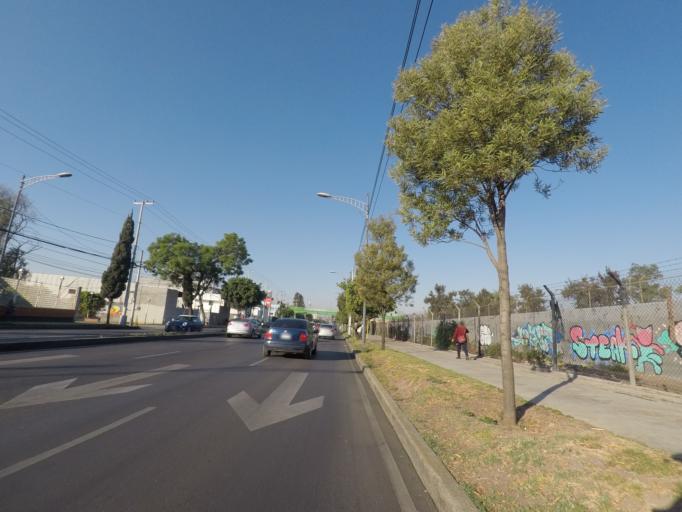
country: MX
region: Mexico City
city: Iztapalapa
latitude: 19.3707
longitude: -99.0834
